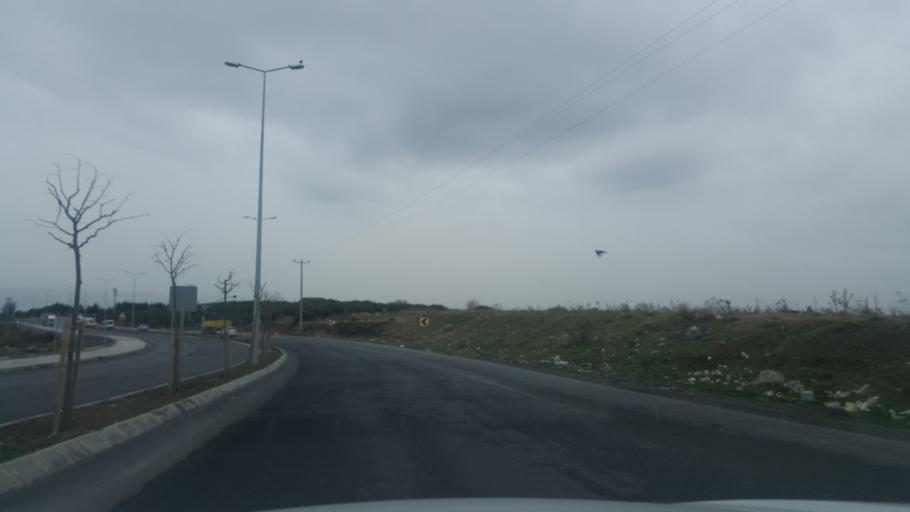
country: TR
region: Kocaeli
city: Tavsancil
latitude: 40.8041
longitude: 29.5515
